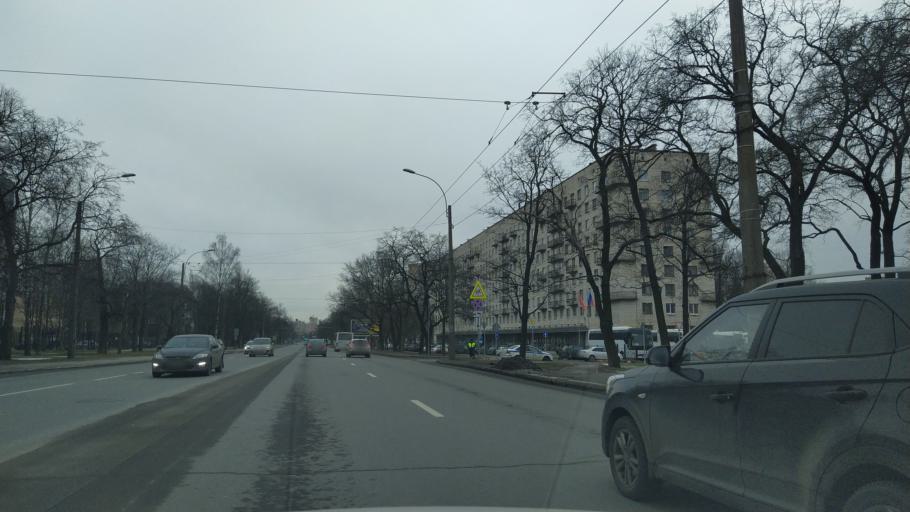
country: RU
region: St.-Petersburg
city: Sosnovka
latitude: 60.0059
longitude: 30.3554
